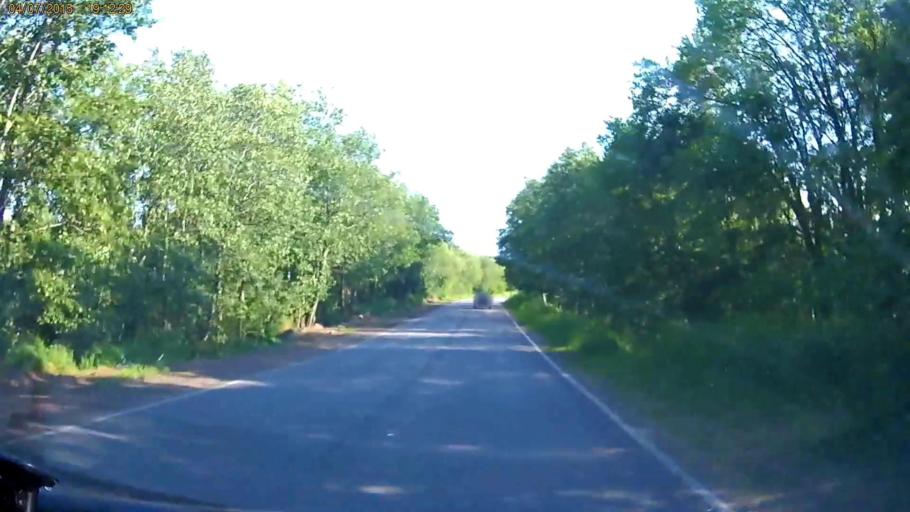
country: RU
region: Leningrad
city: Garbolovo
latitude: 60.3167
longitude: 30.4932
